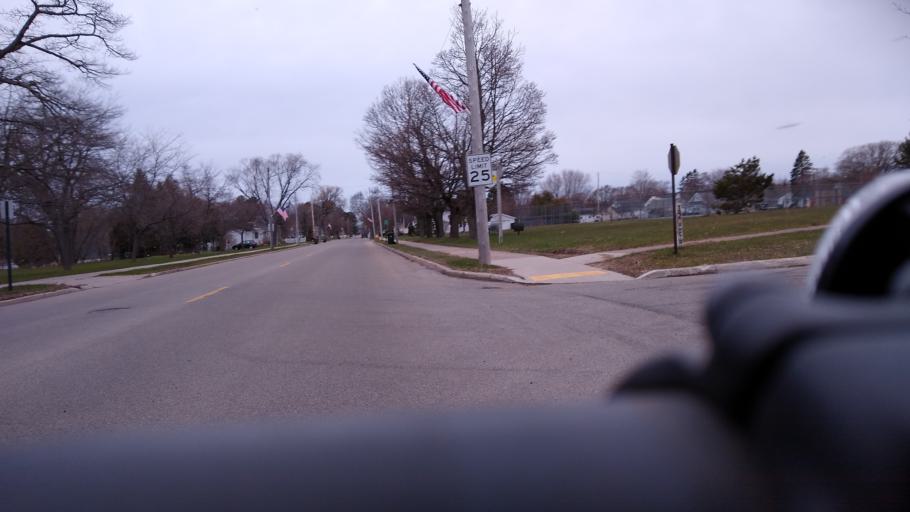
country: US
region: Michigan
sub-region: Delta County
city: Escanaba
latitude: 45.7321
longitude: -87.0631
